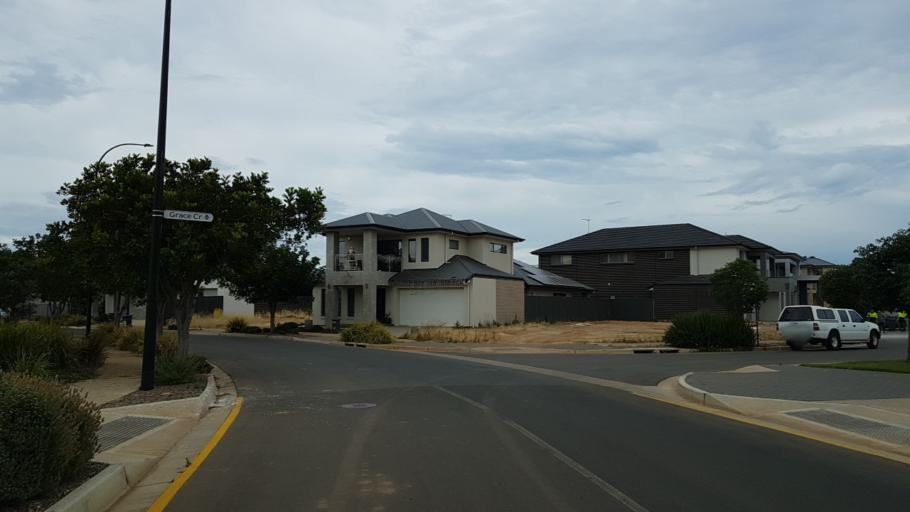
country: AU
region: South Australia
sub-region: Port Adelaide Enfield
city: Alberton
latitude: -34.8661
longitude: 138.5311
